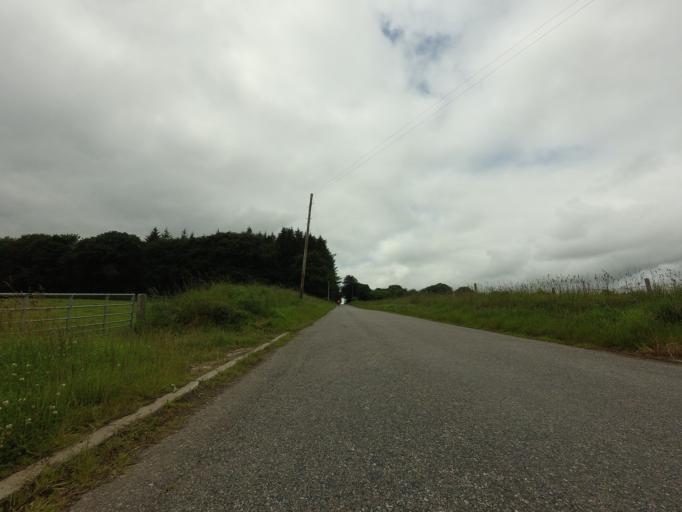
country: GB
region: Scotland
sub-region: Aberdeenshire
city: Mintlaw
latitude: 57.5298
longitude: -2.1493
